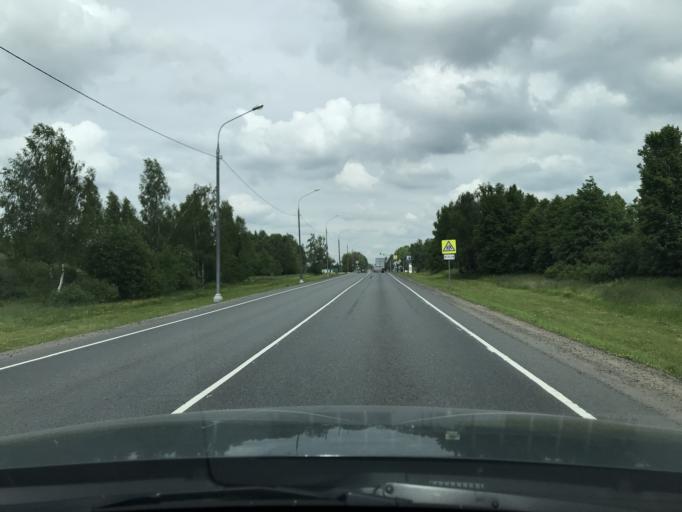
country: RU
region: Moskovskaya
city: Dorokhovo
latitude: 55.3732
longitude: 36.4089
